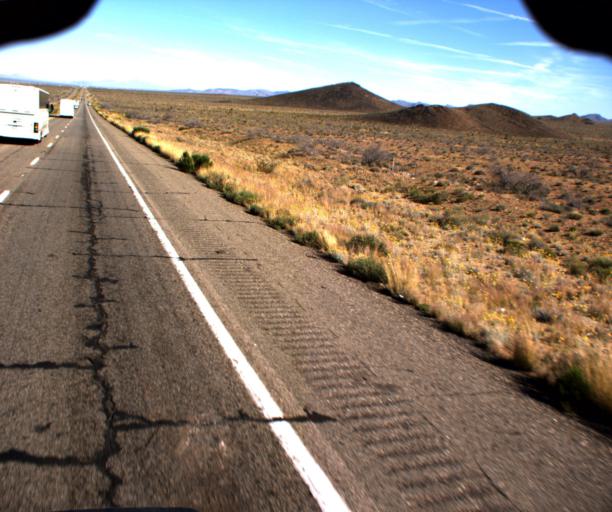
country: US
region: Arizona
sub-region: Mohave County
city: Dolan Springs
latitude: 35.4484
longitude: -114.2960
